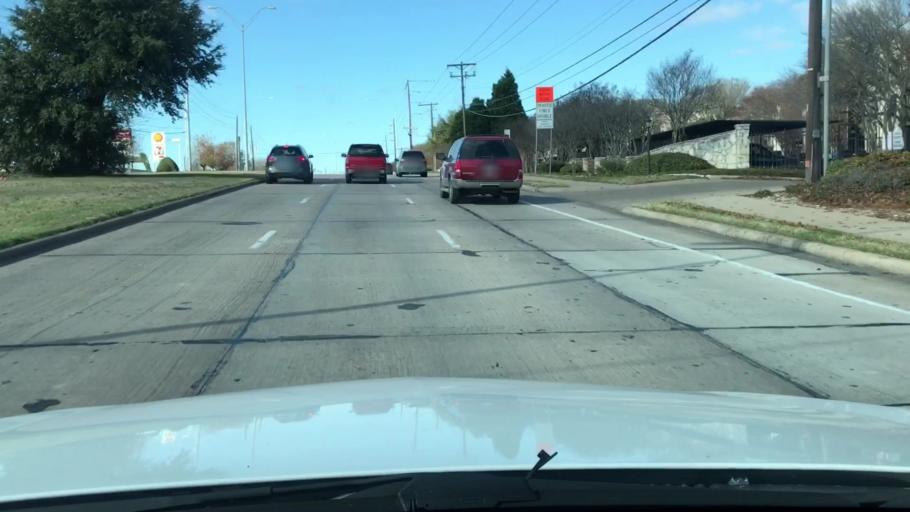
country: US
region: Texas
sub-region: Travis County
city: Onion Creek
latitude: 30.1881
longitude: -97.7639
